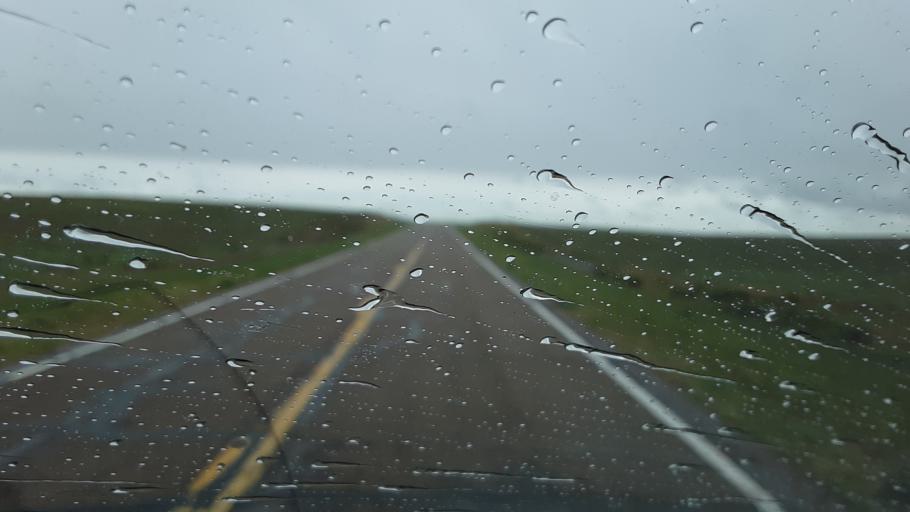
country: US
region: Colorado
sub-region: Lincoln County
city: Hugo
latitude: 38.8496
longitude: -103.2148
